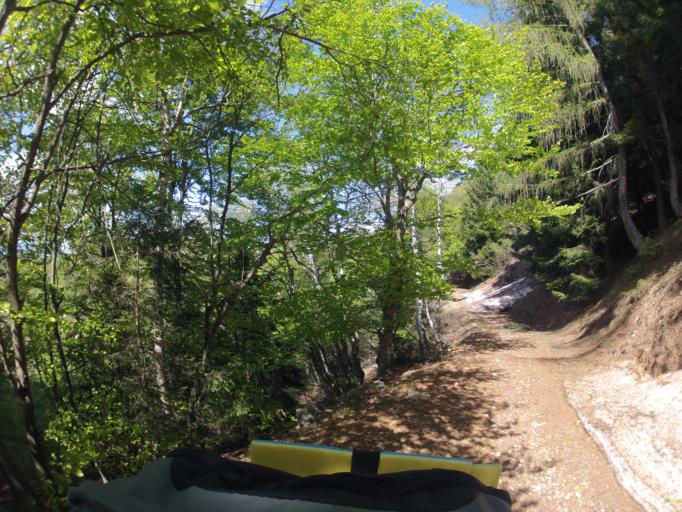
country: IT
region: Piedmont
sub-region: Provincia di Cuneo
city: Peveragno
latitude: 44.2779
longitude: 7.5837
